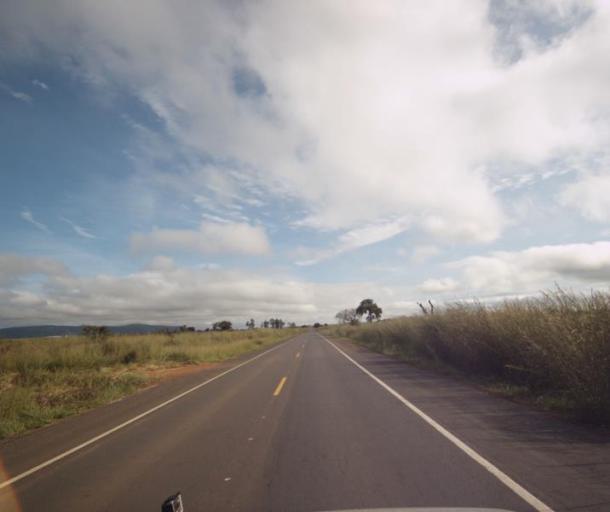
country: BR
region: Goias
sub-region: Padre Bernardo
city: Padre Bernardo
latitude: -15.4510
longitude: -48.6162
